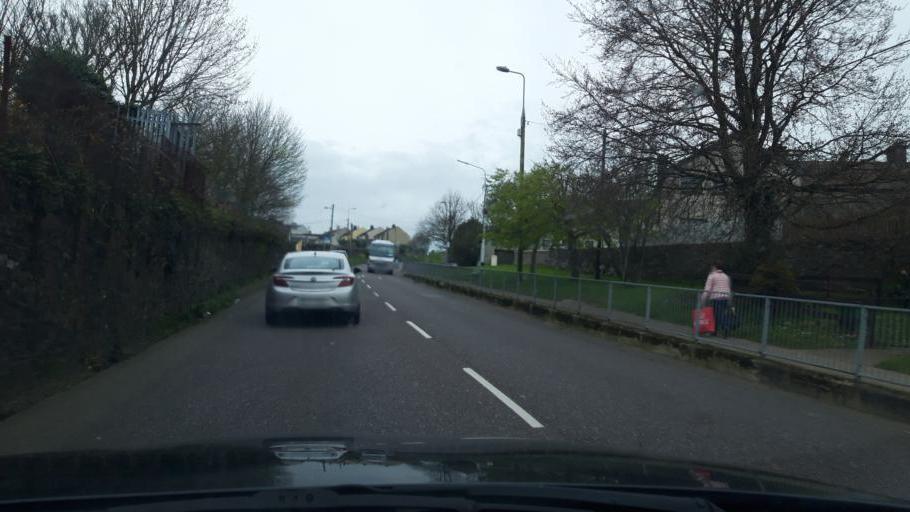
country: IE
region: Munster
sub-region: County Cork
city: Cork
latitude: 51.9170
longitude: -8.4693
